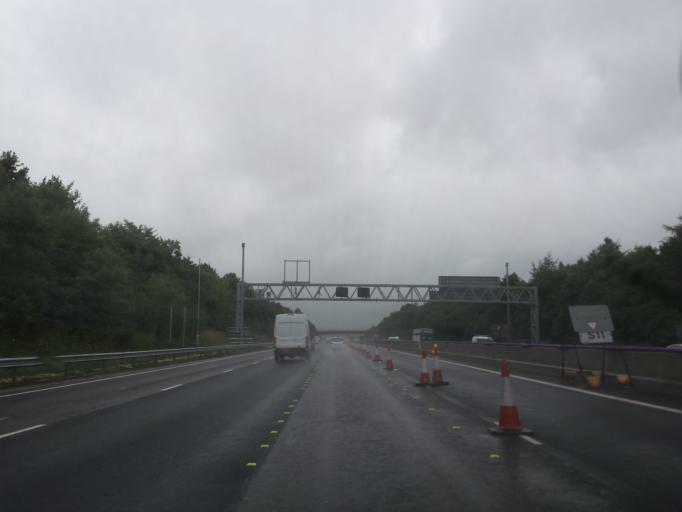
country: GB
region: England
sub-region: Derbyshire
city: Barlborough
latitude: 53.2796
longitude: -1.2990
